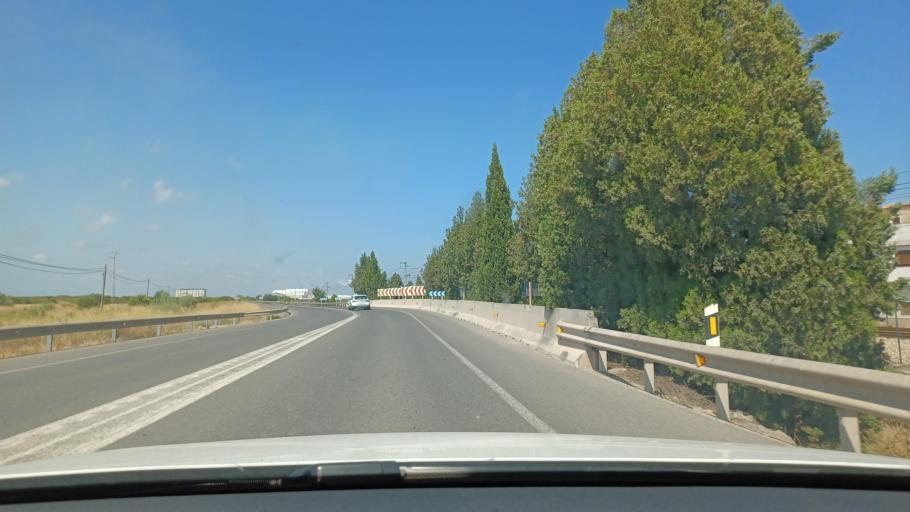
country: ES
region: Valencia
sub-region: Provincia de Castello
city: Chilches
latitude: 39.7838
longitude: -0.1899
